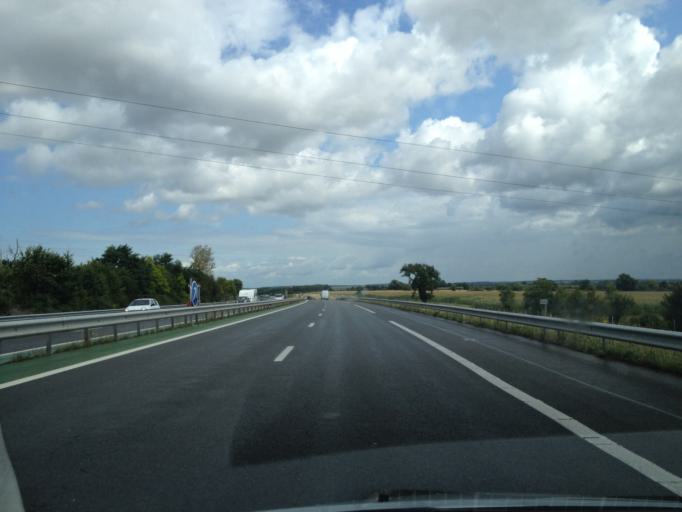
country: FR
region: Pays de la Loire
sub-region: Departement de Maine-et-Loire
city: Saint-Lambert-du-Lattay
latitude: 47.2582
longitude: -0.6176
